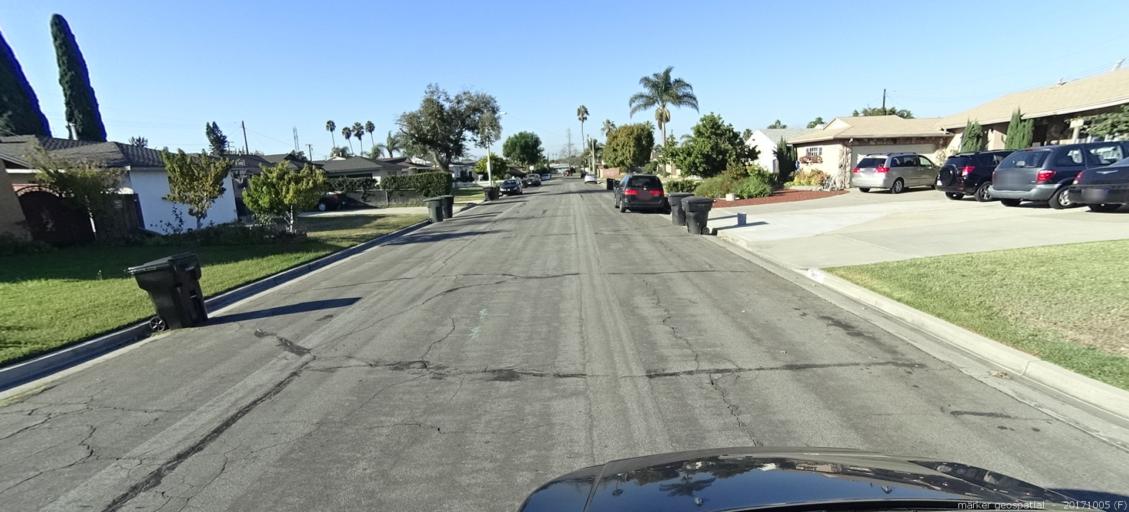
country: US
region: California
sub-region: Orange County
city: Stanton
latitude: 33.7908
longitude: -117.9782
